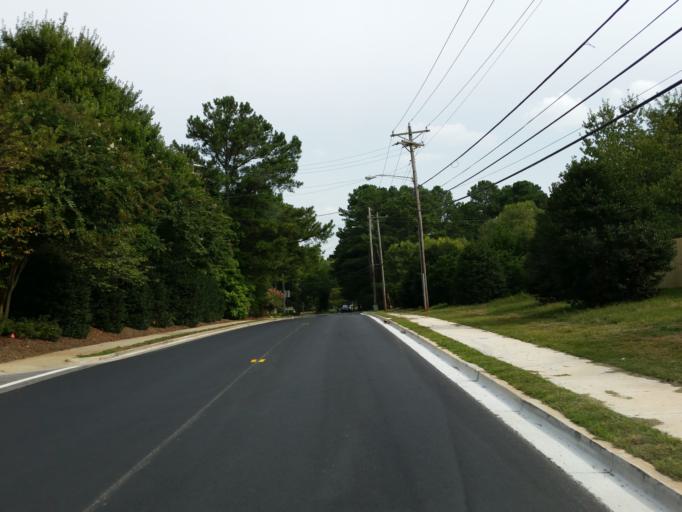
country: US
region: Georgia
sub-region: Cherokee County
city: Woodstock
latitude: 34.0300
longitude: -84.4950
